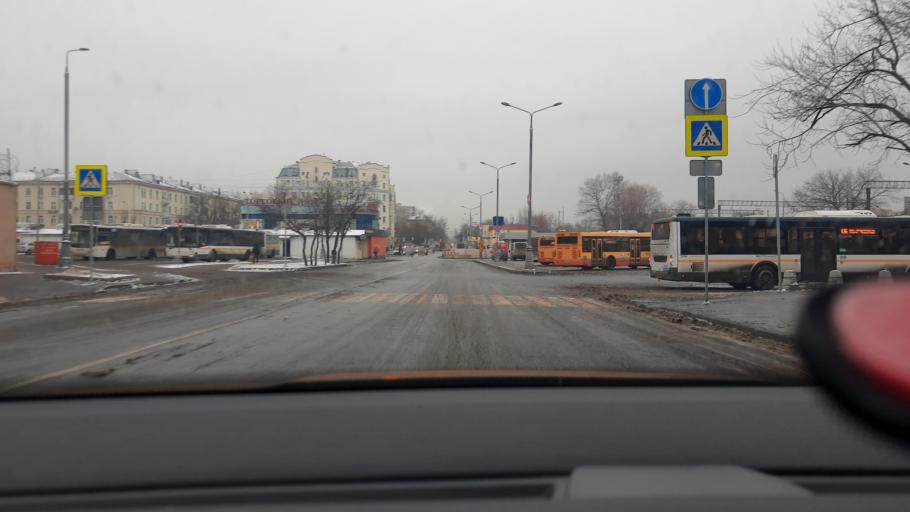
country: RU
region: Moscow
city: Pokrovskoye-Streshnevo
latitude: 55.8267
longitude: 37.4399
